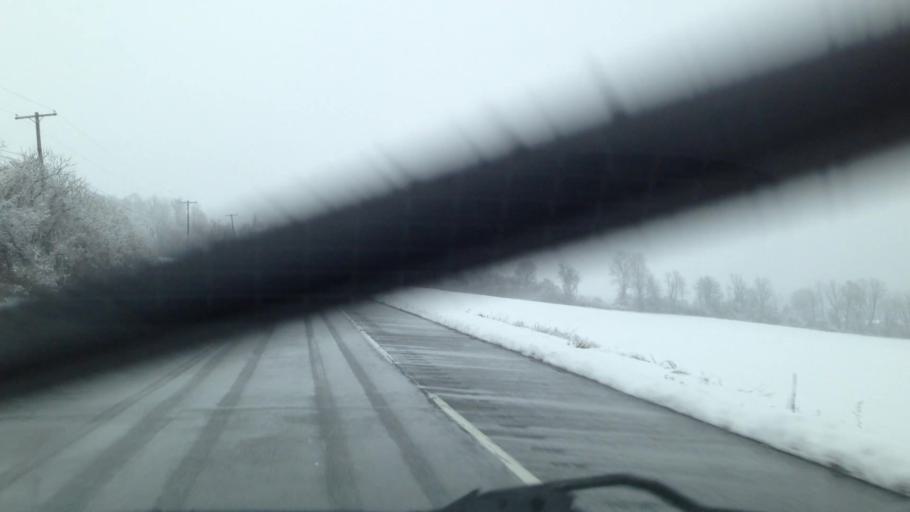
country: US
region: New York
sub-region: Onondaga County
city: Peru
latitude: 43.0350
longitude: -76.3882
